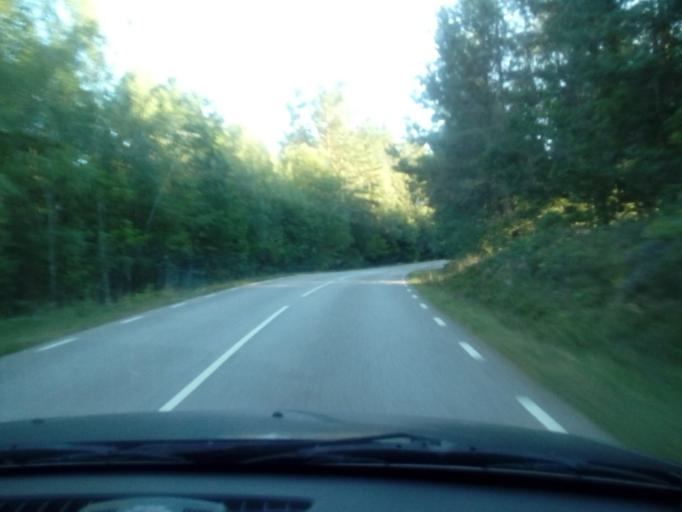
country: SE
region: Kalmar
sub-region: Vasterviks Kommun
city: Gamleby
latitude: 57.8088
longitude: 16.4345
